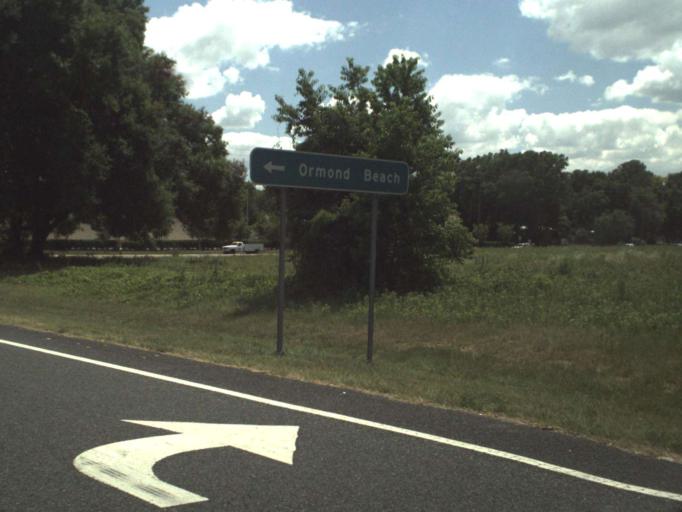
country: US
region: Florida
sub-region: Marion County
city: Ocala
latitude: 29.2606
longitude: -82.1522
